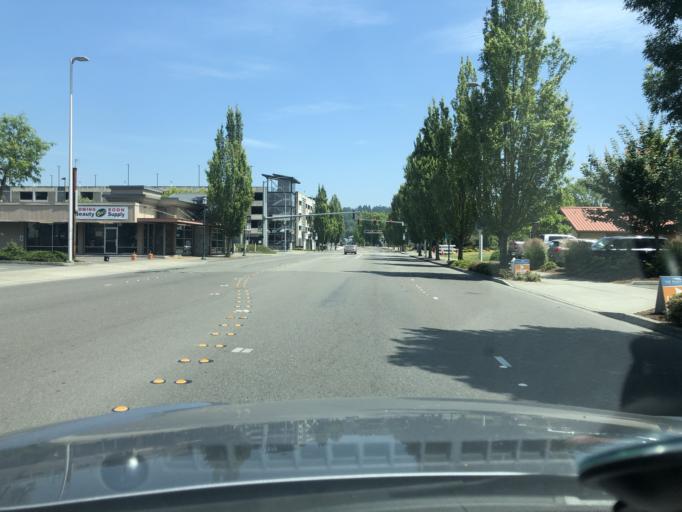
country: US
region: Washington
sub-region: King County
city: Kent
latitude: 47.3830
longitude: -122.2362
